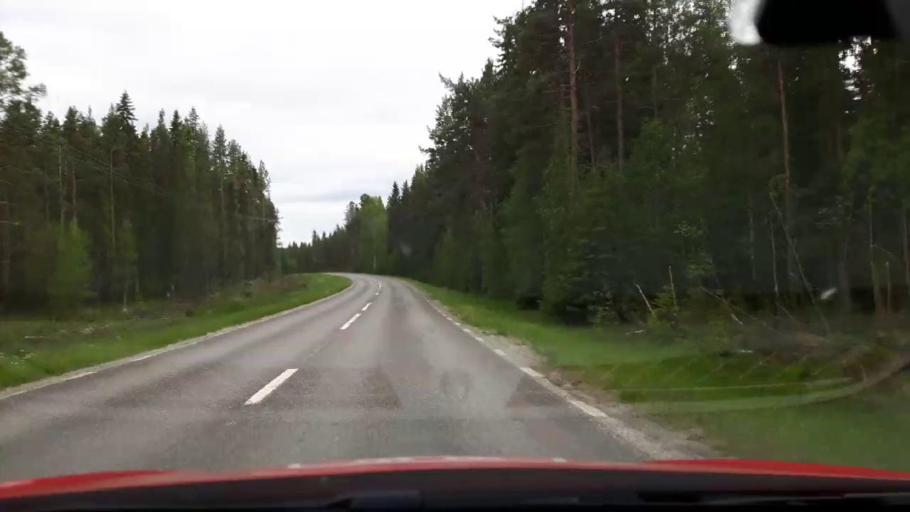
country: SE
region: Jaemtland
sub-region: Ragunda Kommun
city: Hammarstrand
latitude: 63.0825
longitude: 16.3674
